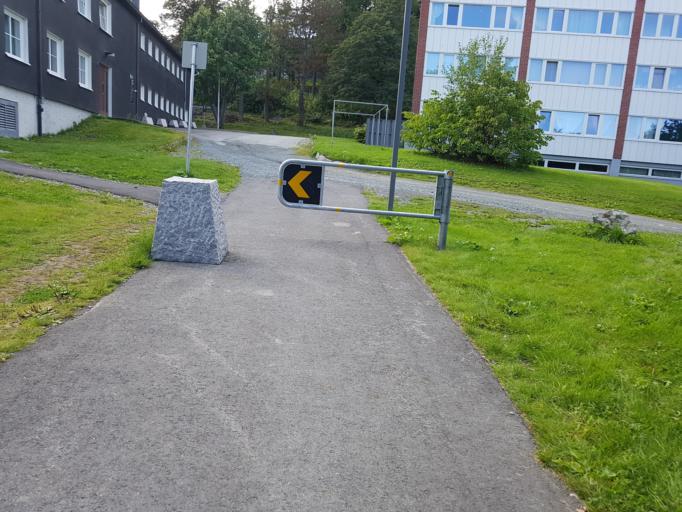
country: NO
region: Sor-Trondelag
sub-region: Trondheim
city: Trondheim
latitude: 63.4296
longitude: 10.4390
